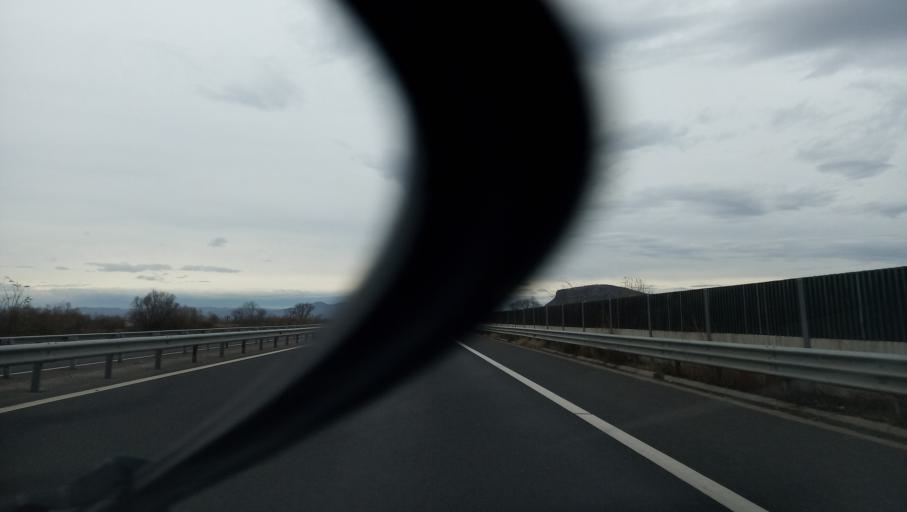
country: RO
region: Hunedoara
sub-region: Comuna Turdas
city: Turdas
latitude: 45.8405
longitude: 23.0866
